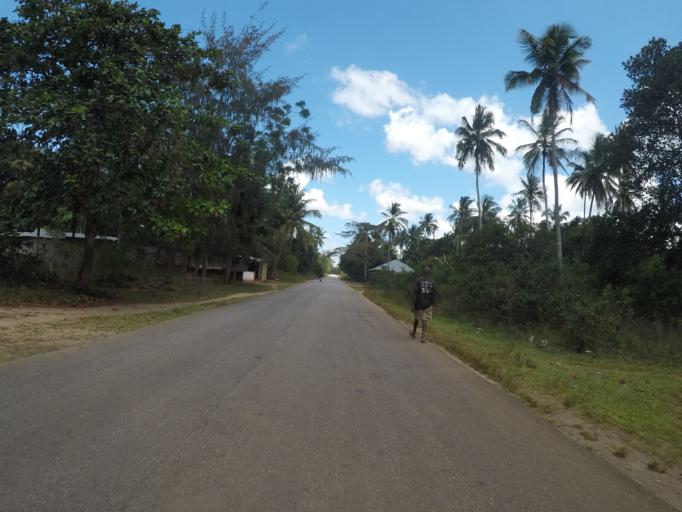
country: TZ
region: Zanzibar Central/South
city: Koani
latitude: -6.1533
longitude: 39.3399
